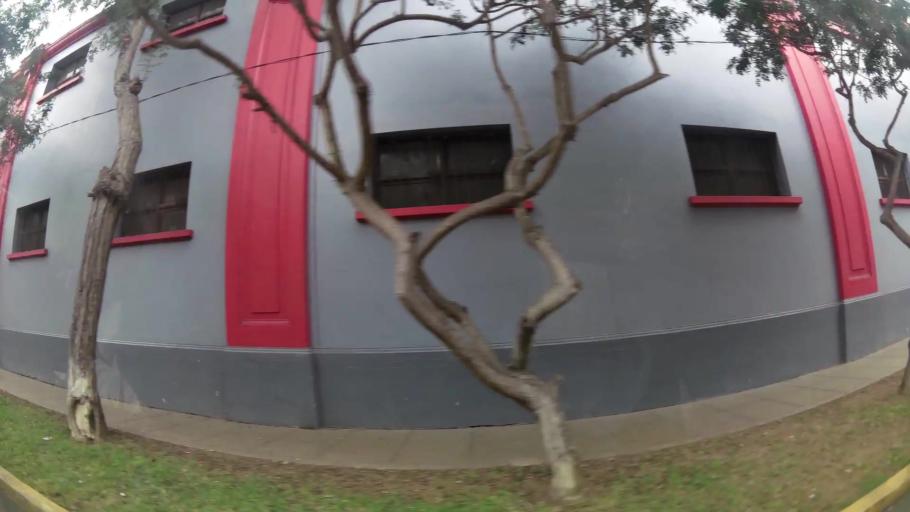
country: PE
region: Lima
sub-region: Lima
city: San Isidro
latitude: -12.1175
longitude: -77.0414
